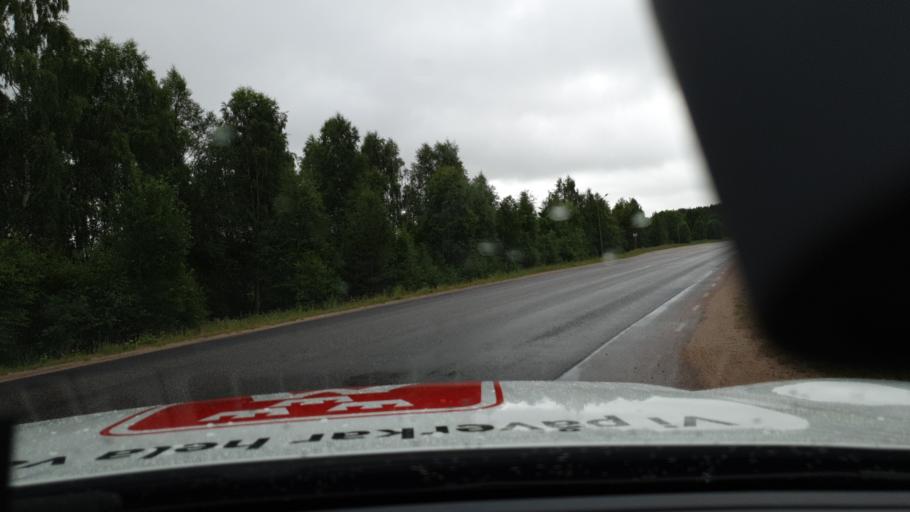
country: SE
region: Norrbotten
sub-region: Overtornea Kommun
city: OEvertornea
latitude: 66.4574
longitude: 23.6278
